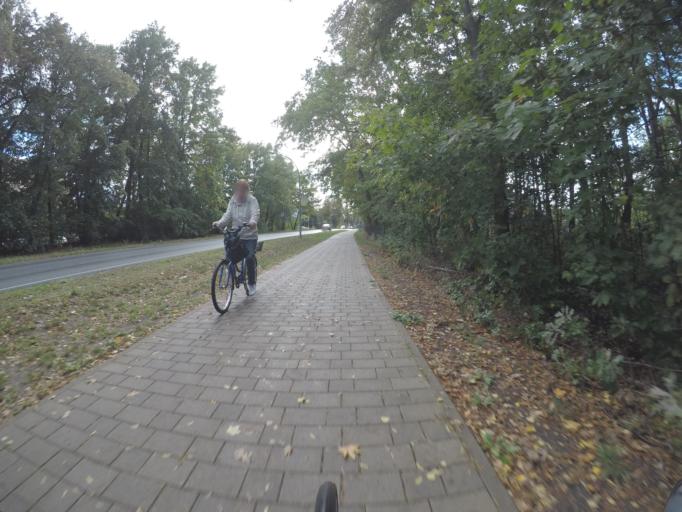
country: DE
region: Brandenburg
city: Strausberg
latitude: 52.5475
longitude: 13.8613
